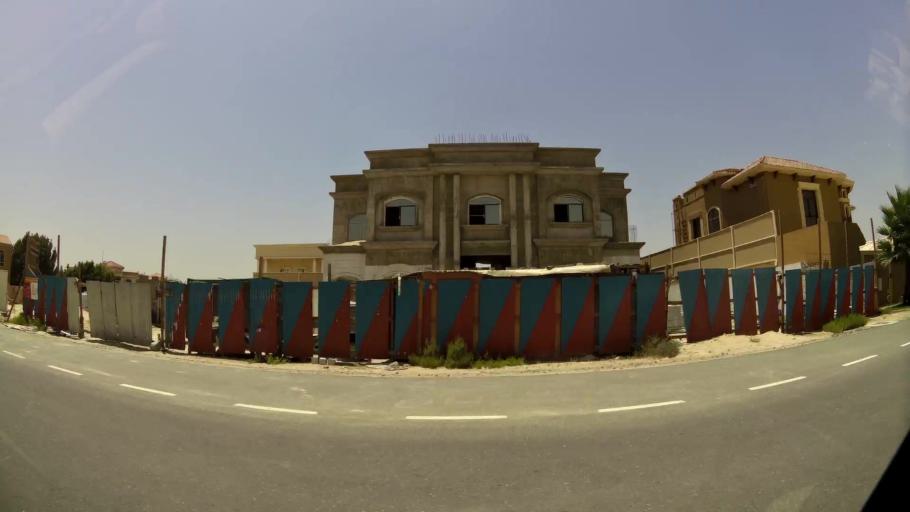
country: AE
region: Dubai
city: Dubai
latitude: 25.0882
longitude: 55.2096
